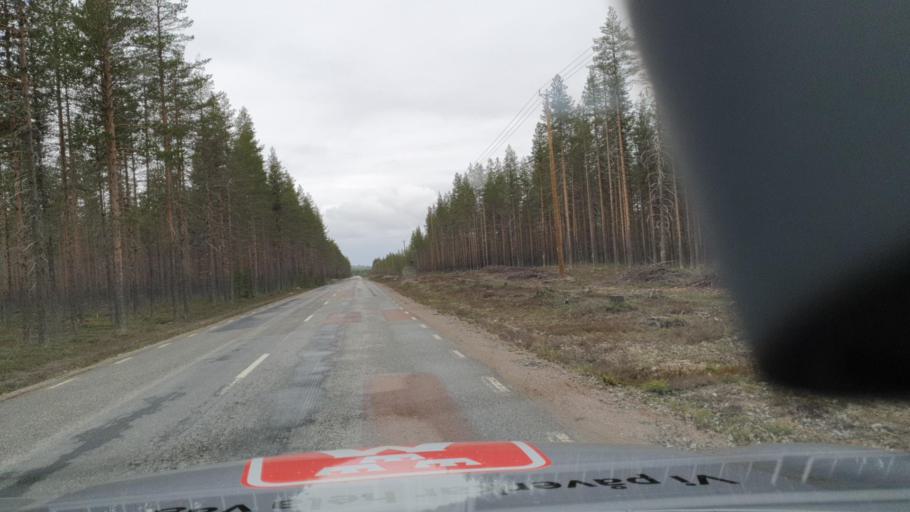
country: SE
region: Vaesternorrland
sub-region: Solleftea Kommun
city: Solleftea
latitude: 63.6154
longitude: 17.4938
